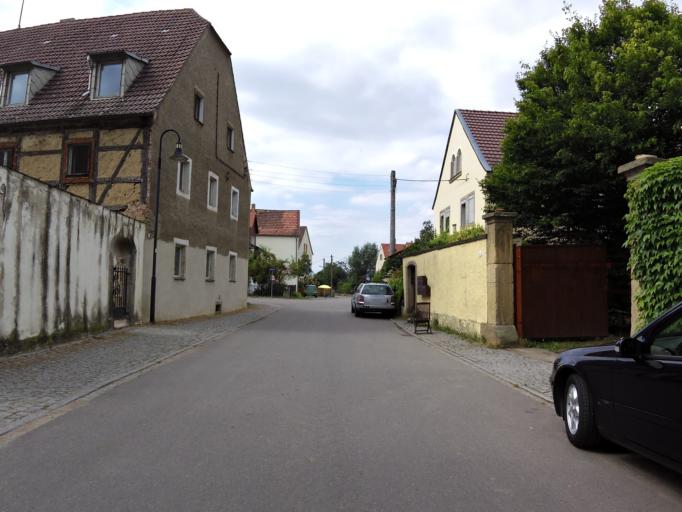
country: DE
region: Saxony
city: Radebeul
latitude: 51.0944
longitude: 13.6429
